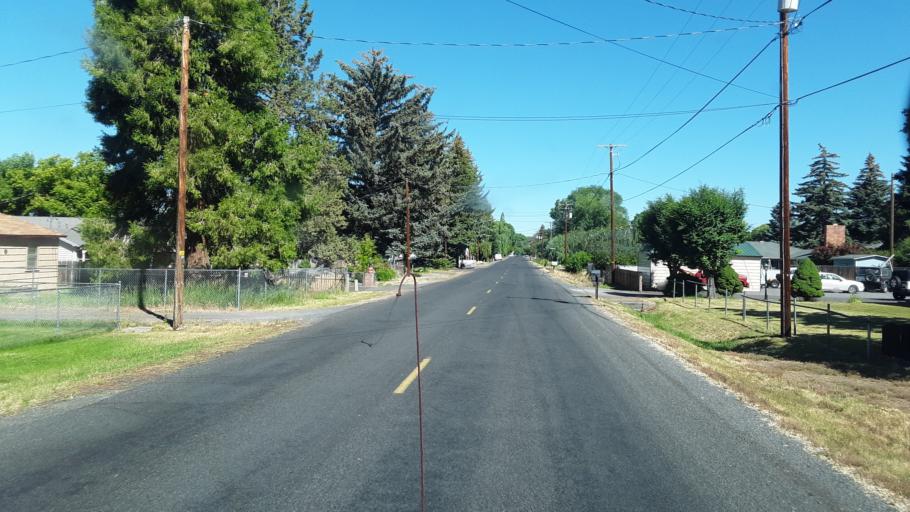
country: US
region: Oregon
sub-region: Klamath County
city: Altamont
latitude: 42.1944
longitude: -121.7244
